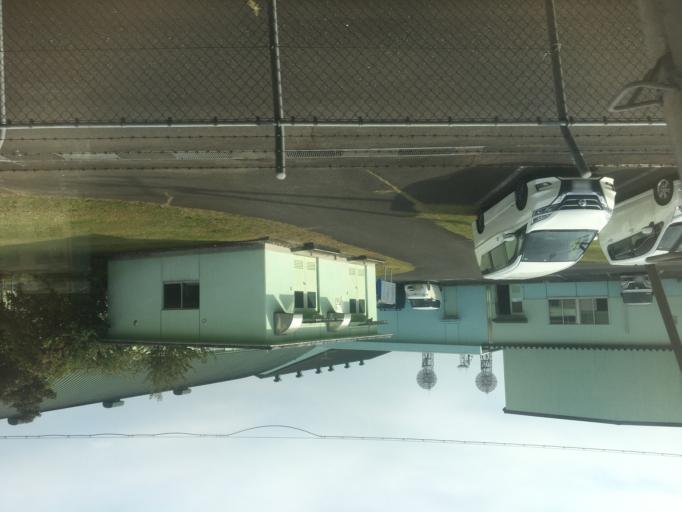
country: JP
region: Saitama
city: Sayama
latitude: 35.8434
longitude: 139.4021
